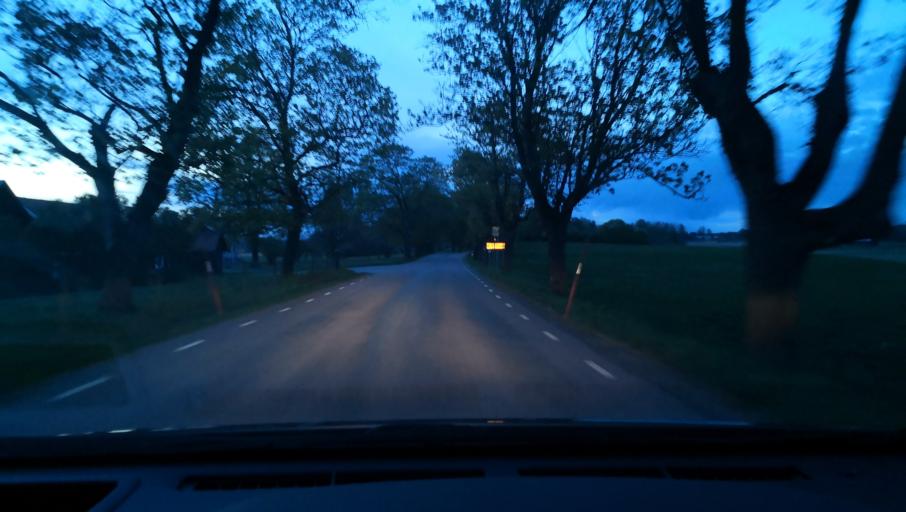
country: SE
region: OErebro
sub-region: Askersunds Kommun
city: Asbro
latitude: 59.0977
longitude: 15.0066
